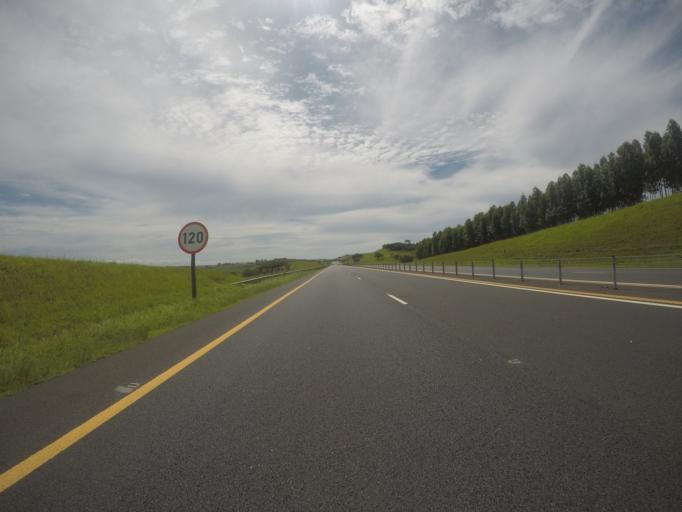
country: ZA
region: KwaZulu-Natal
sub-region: iLembe District Municipality
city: Mandeni
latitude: -29.1804
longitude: 31.4953
